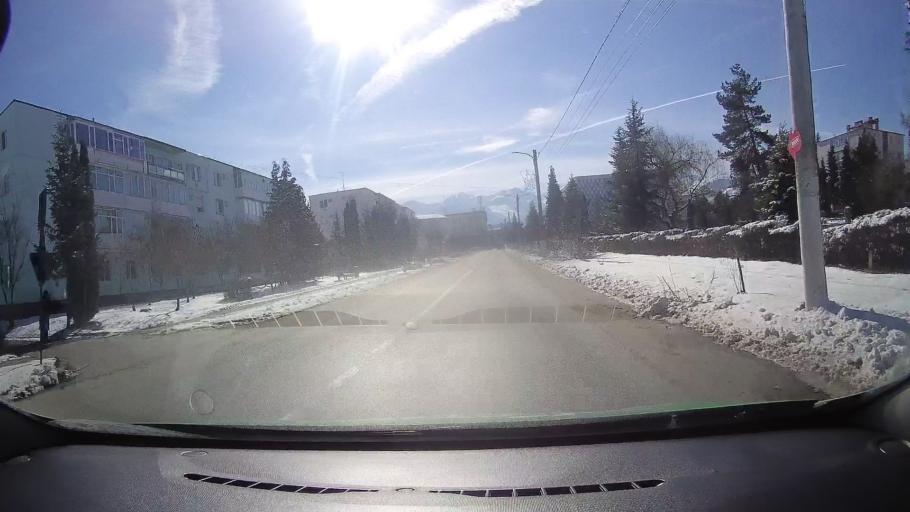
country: RO
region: Brasov
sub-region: Oras Victoria
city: Victoria
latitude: 45.7317
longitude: 24.7013
